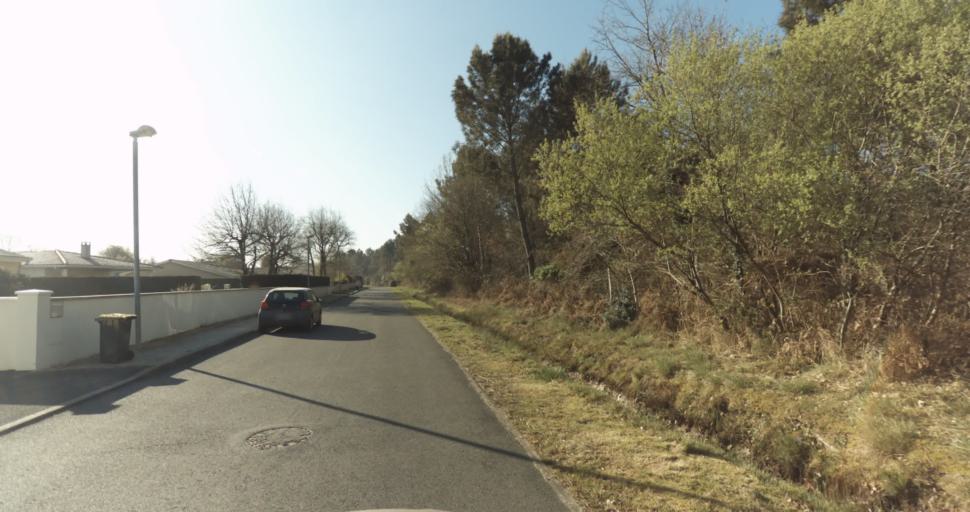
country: FR
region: Aquitaine
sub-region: Departement de la Gironde
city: Martignas-sur-Jalle
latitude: 44.8017
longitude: -0.7955
